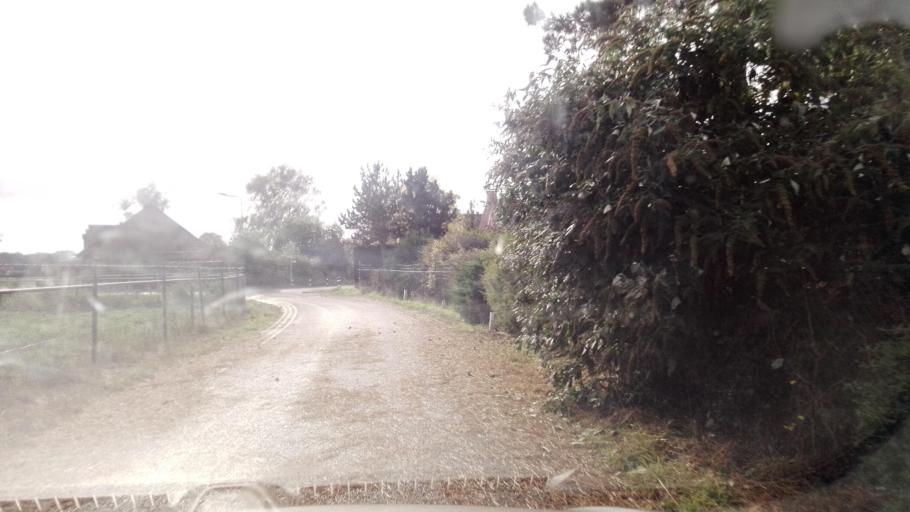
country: NL
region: Limburg
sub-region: Gemeente Venlo
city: Venlo
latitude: 51.4157
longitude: 6.1765
